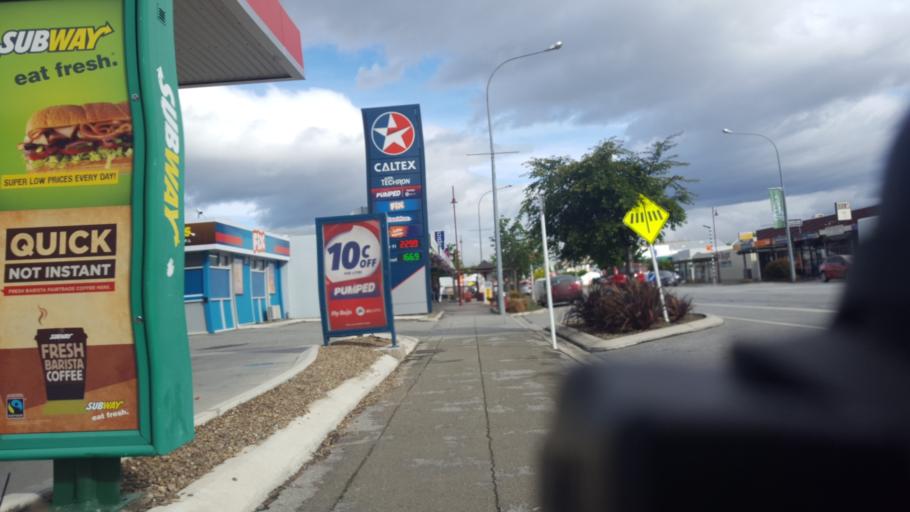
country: NZ
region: Otago
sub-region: Queenstown-Lakes District
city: Wanaka
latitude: -45.2525
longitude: 169.3892
